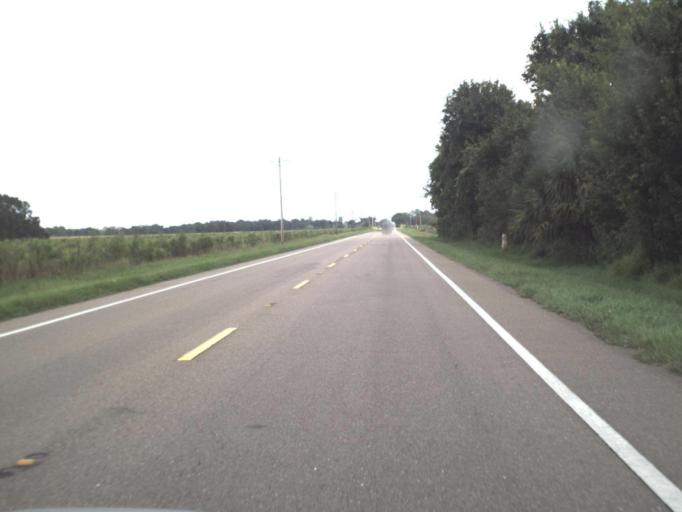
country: US
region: Florida
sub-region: Hardee County
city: Zolfo Springs
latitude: 27.4823
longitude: -81.8973
